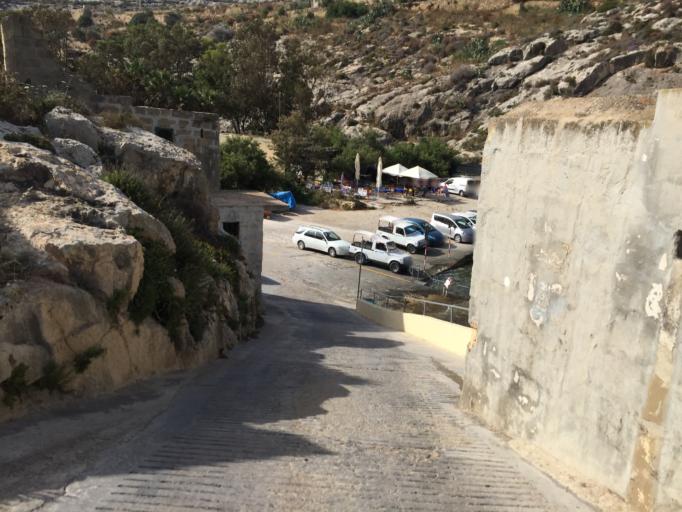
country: MT
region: Ghajnsielem
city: Ghajnsielem
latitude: 36.0199
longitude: 14.2711
